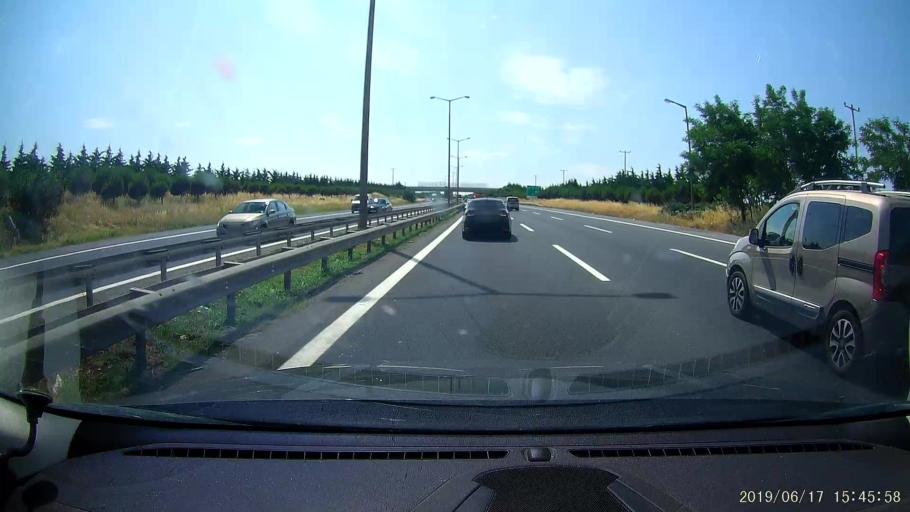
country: TR
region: Istanbul
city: Silivri
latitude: 41.1228
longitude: 28.2402
